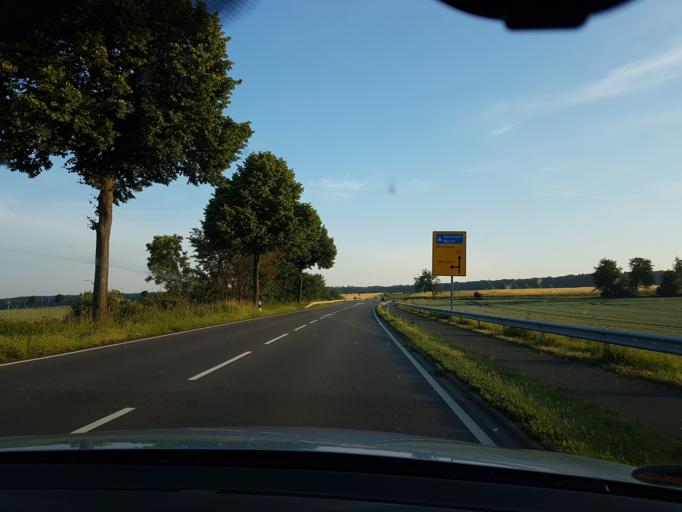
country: DE
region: Lower Saxony
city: Wolsdorf
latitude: 52.1935
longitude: 10.9696
